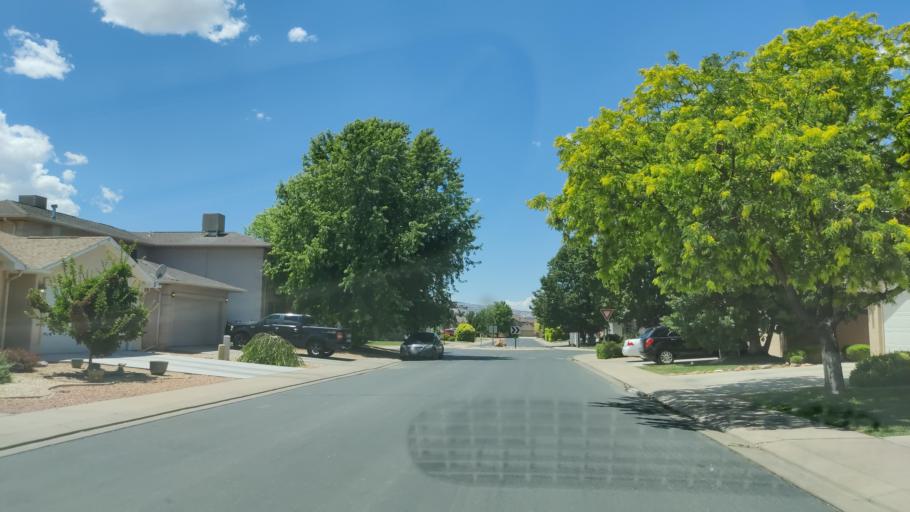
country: US
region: Colorado
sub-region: Mesa County
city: Redlands
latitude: 39.1096
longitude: -108.6001
